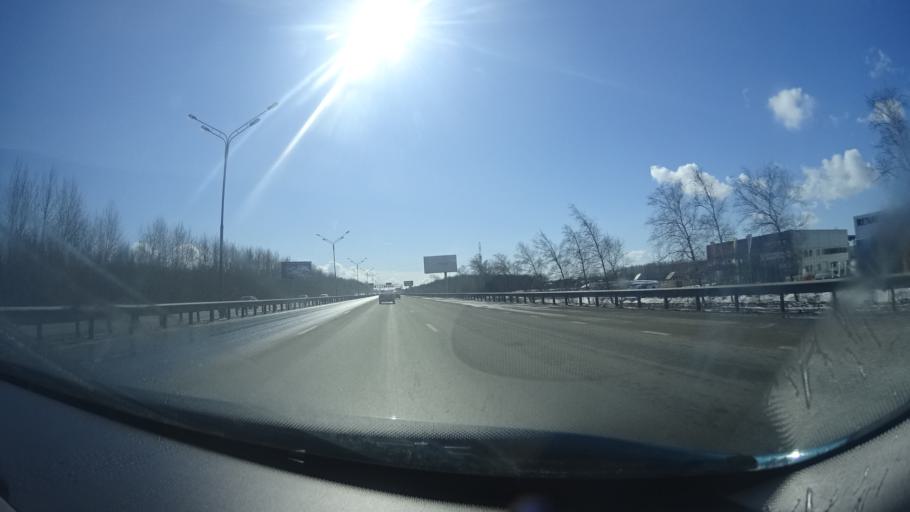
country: RU
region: Bashkortostan
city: Ufa
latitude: 54.6678
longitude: 55.9337
